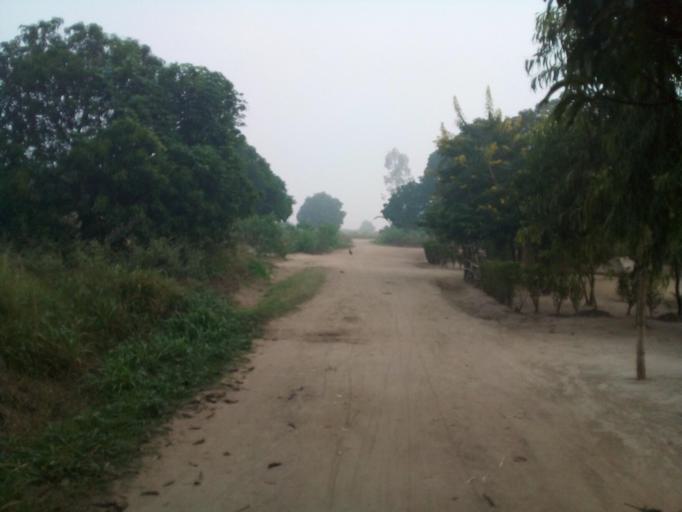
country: MZ
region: Zambezia
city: Quelimane
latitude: -17.5933
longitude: 36.6857
